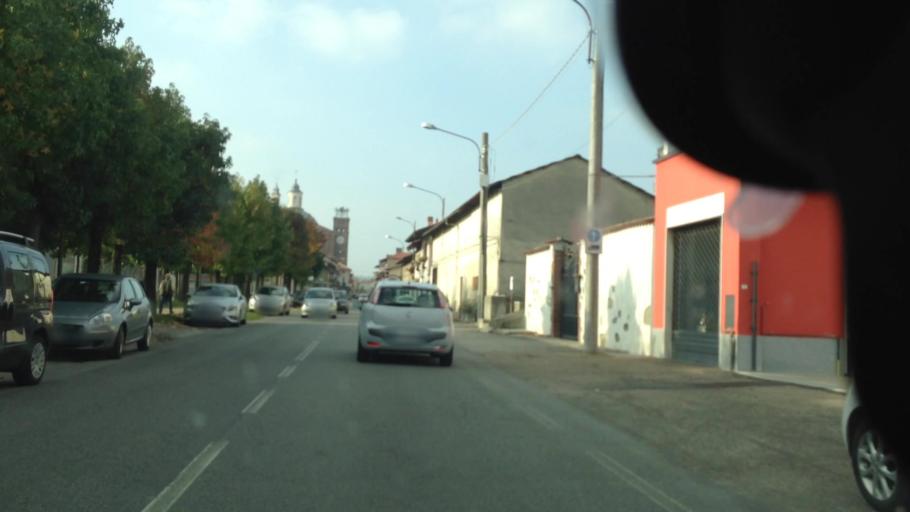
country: IT
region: Piedmont
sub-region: Provincia di Vercelli
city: Borgo d'Ale
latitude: 45.3474
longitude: 8.0569
